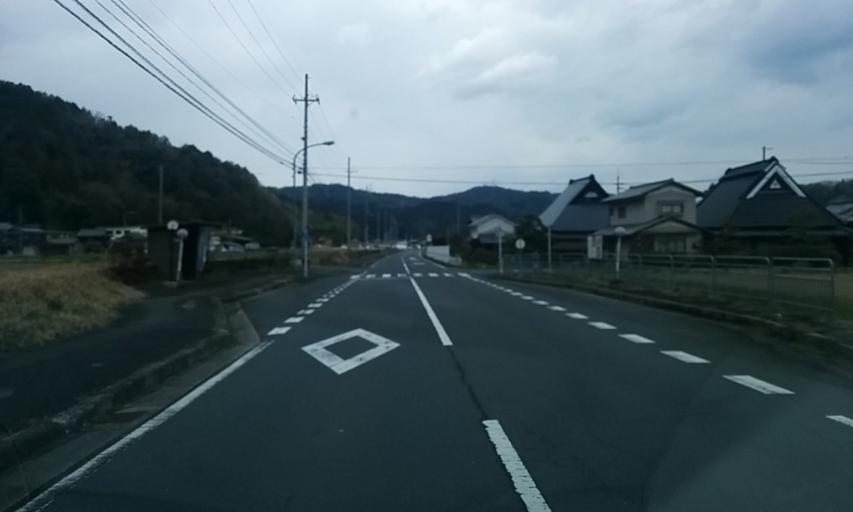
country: JP
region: Kyoto
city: Kameoka
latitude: 35.0957
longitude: 135.4437
